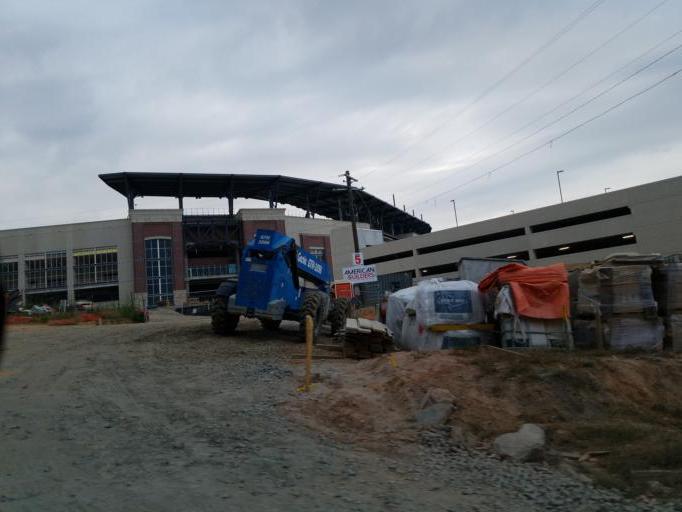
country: US
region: Georgia
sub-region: Cobb County
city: Vinings
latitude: 33.8913
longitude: -84.4650
